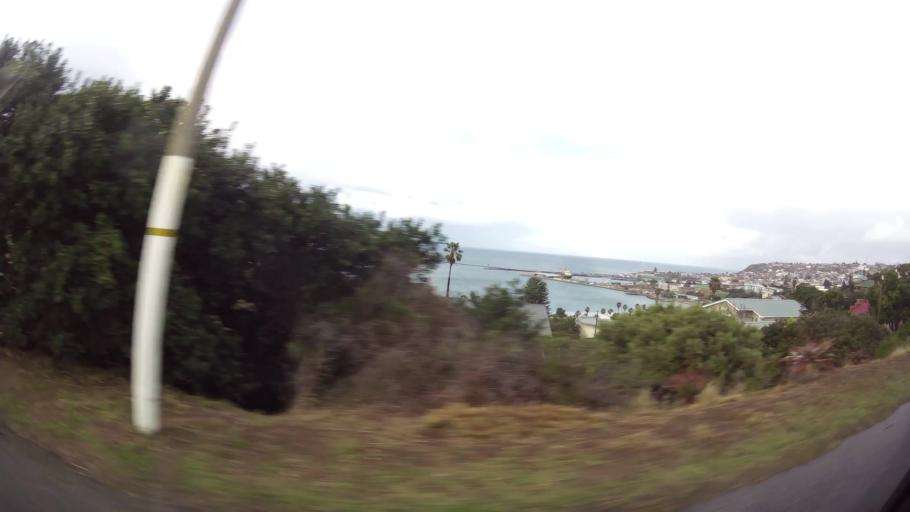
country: ZA
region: Western Cape
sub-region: Eden District Municipality
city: Mossel Bay
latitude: -34.1775
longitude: 22.1322
